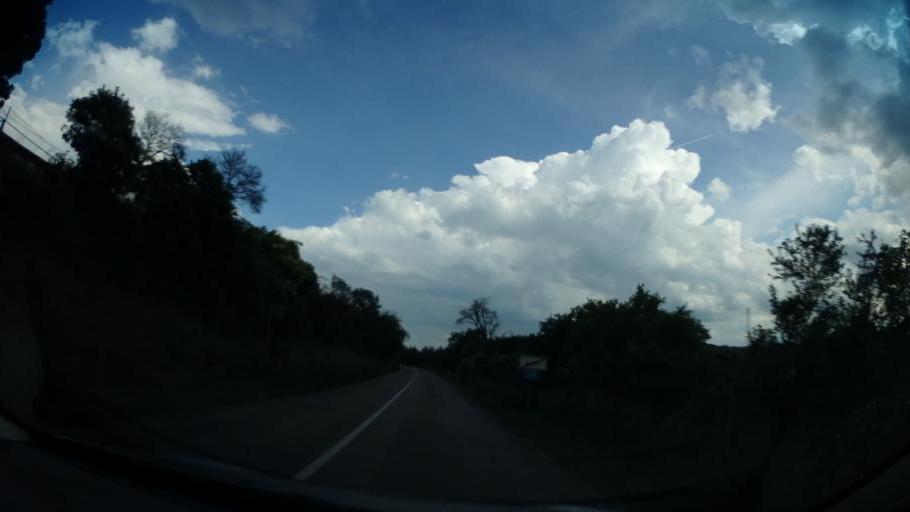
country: CZ
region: South Moravian
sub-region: Okres Brno-Venkov
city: Dolni Loucky
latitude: 49.3765
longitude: 16.3556
